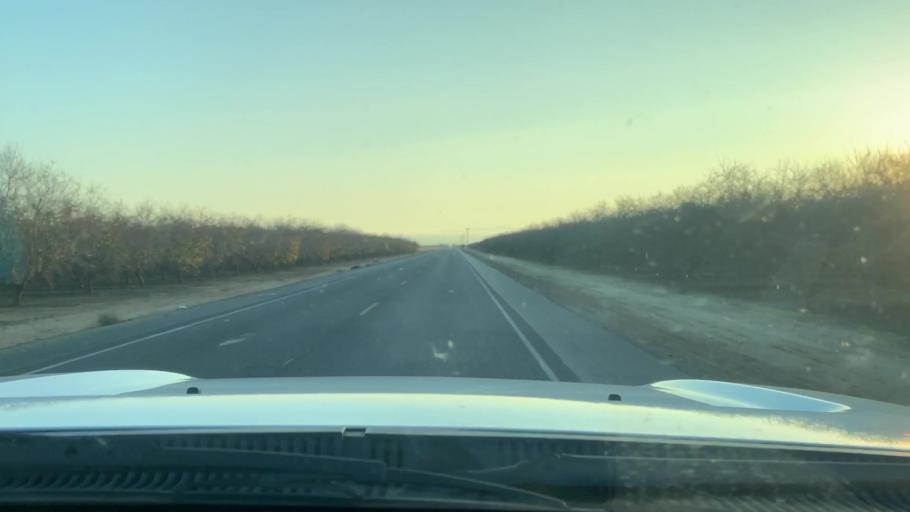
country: US
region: California
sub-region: Kern County
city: Wasco
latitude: 35.5003
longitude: -119.3942
